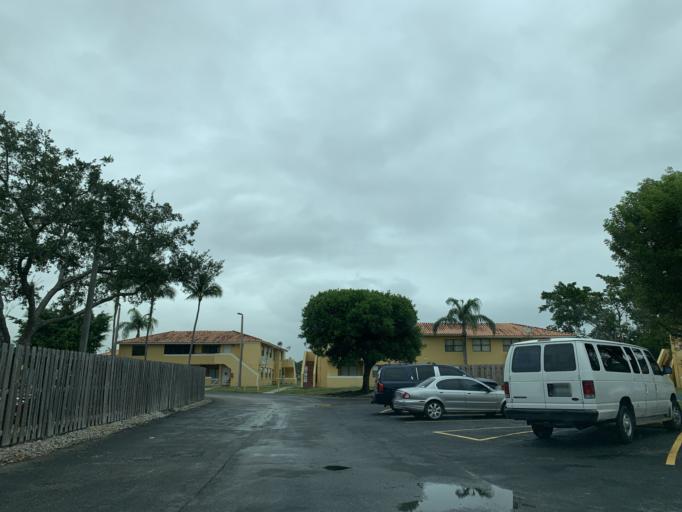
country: US
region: Florida
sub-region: Miami-Dade County
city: Kendall West
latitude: 25.6926
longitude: -80.4339
